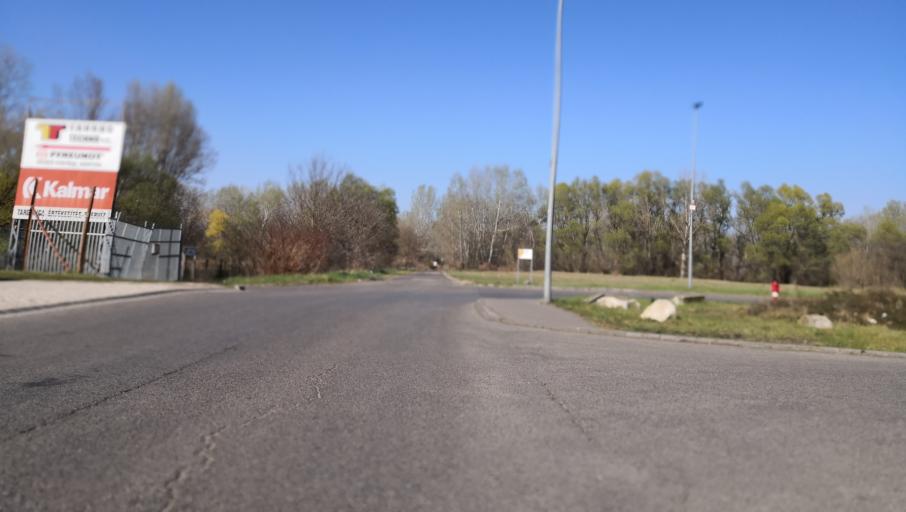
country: HU
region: Budapest
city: Budapest XVII. keruelet
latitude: 47.4851
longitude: 19.2349
